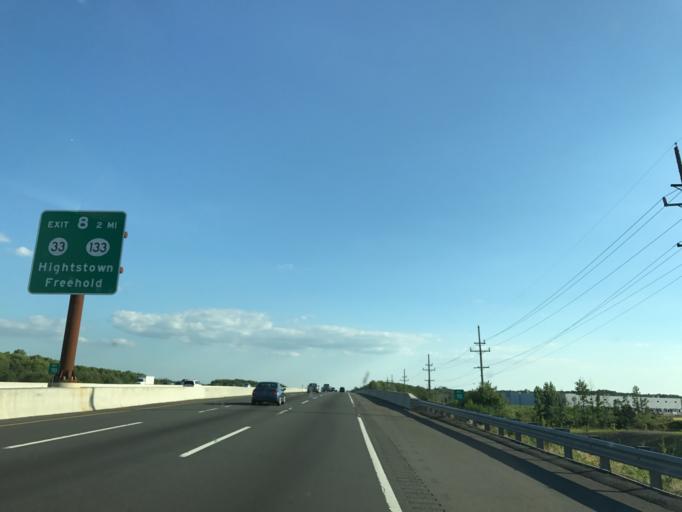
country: US
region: New Jersey
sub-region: Middlesex County
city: Cranbury
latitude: 40.2982
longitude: -74.4970
